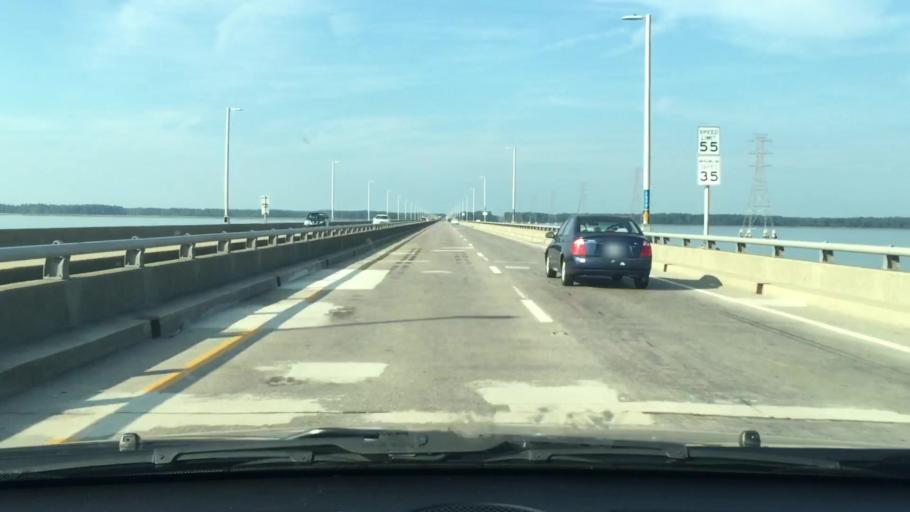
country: US
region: Virginia
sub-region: City of Newport News
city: Newport News
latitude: 36.9828
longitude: -76.4934
